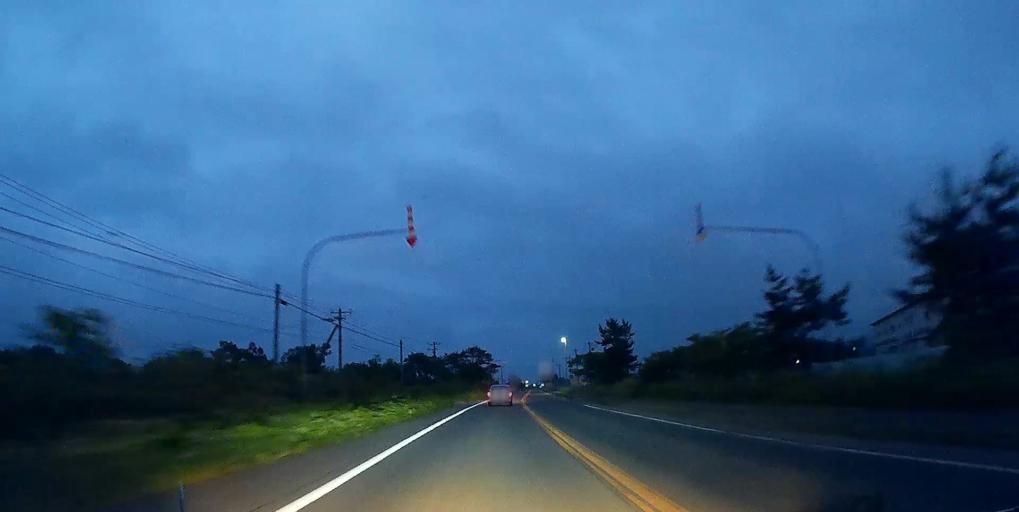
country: JP
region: Hokkaido
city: Nanae
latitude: 42.2214
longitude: 140.3725
